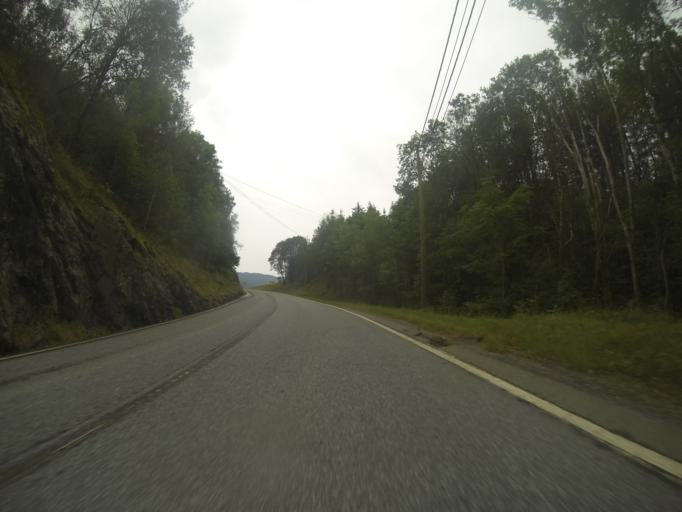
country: NO
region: Rogaland
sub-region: Suldal
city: Sand
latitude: 59.4842
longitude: 6.2017
